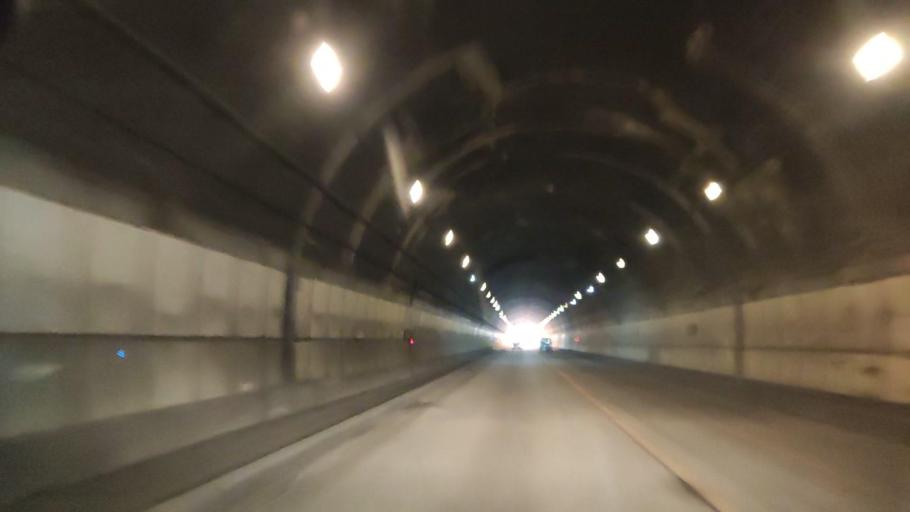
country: JP
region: Aomori
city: Aomori Shi
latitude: 40.8585
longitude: 140.8422
